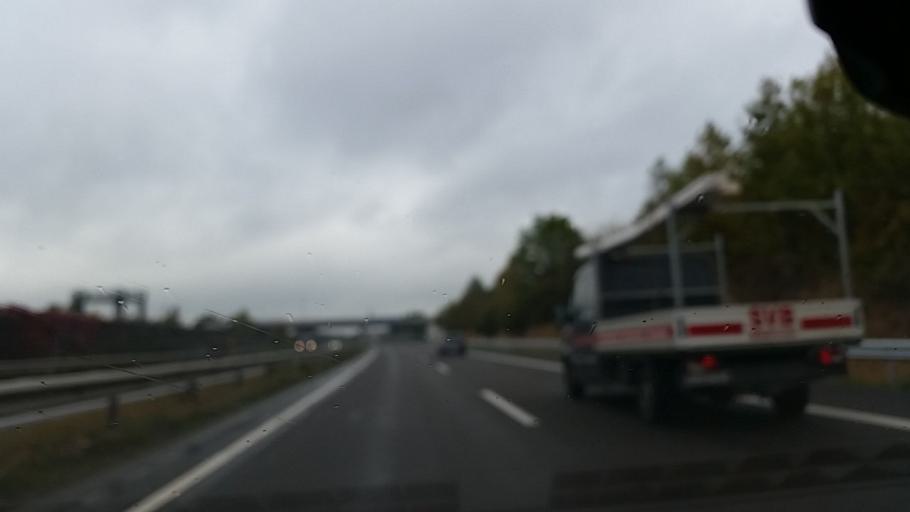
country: DE
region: Lower Saxony
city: Bardowick
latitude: 53.2878
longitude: 10.3798
